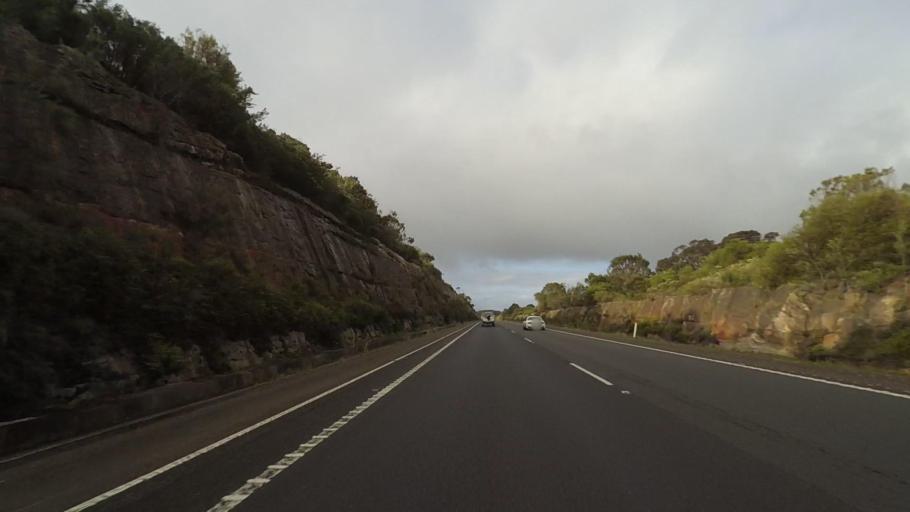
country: AU
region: New South Wales
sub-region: Wollongong
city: Bulli
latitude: -34.2576
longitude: 150.9309
